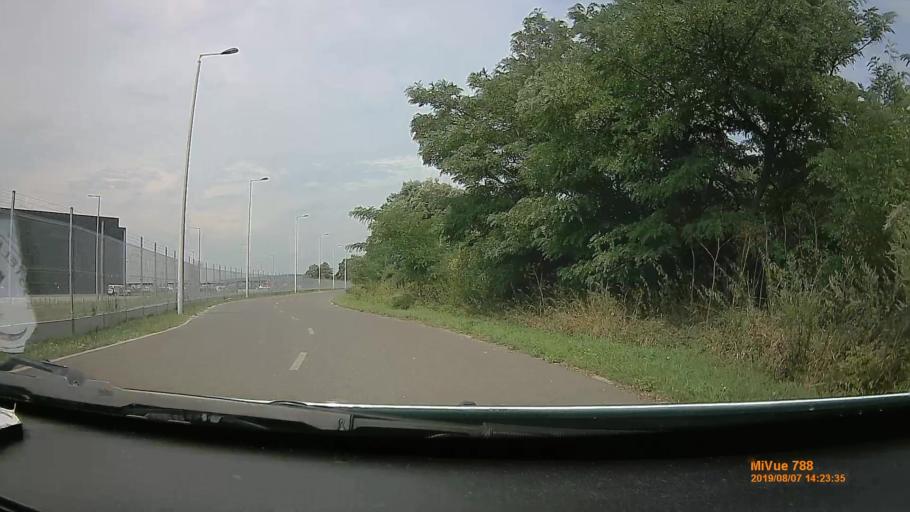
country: HU
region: Borsod-Abauj-Zemplen
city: Szikszo
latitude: 48.1737
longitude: 20.9241
